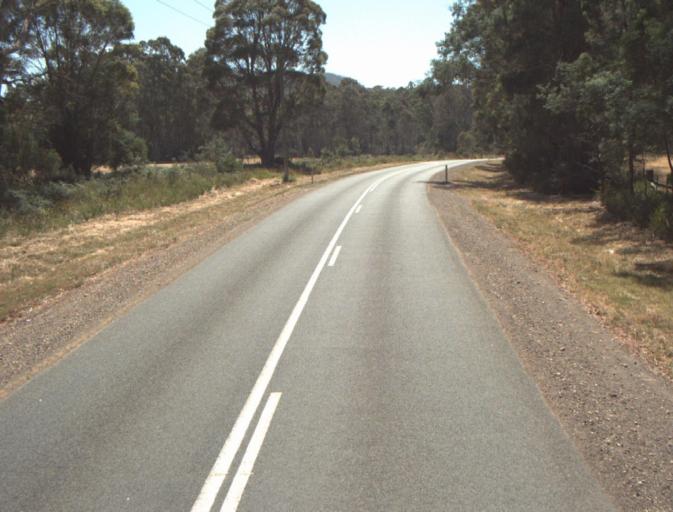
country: AU
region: Tasmania
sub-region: Launceston
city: Mayfield
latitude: -41.2853
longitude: 147.1266
